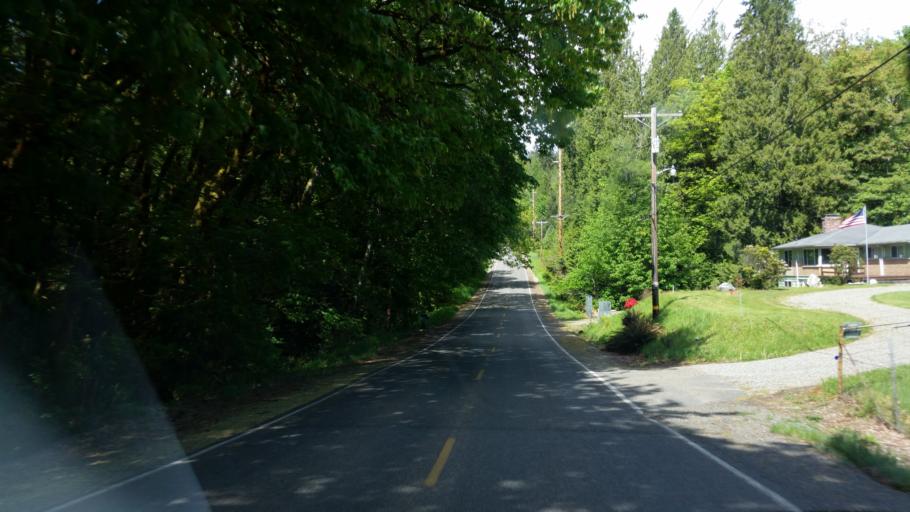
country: US
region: Washington
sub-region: Pierce County
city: Key Center
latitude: 47.3162
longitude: -122.7696
